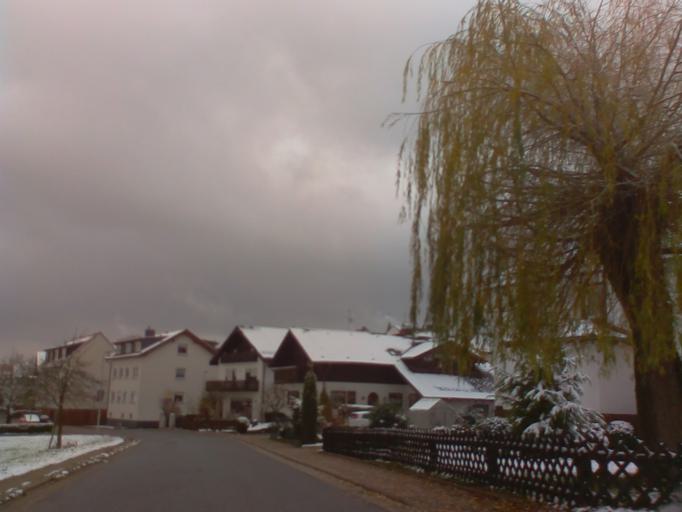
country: DE
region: Hesse
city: Unter-Abtsteinach
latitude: 49.5466
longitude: 8.7875
